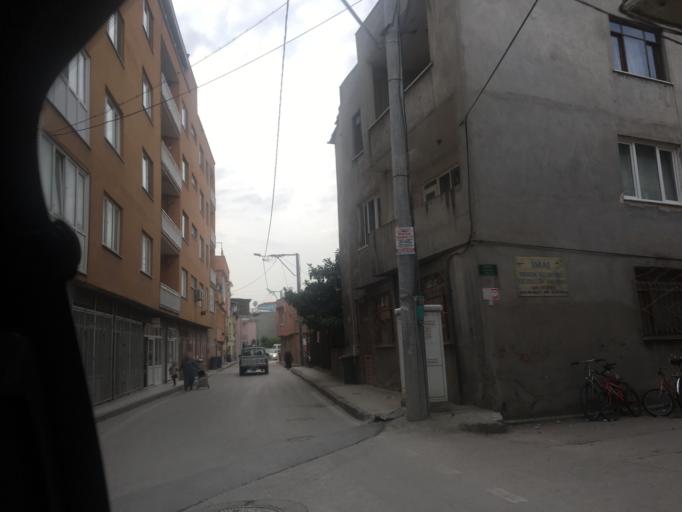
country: TR
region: Bursa
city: Yildirim
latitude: 40.2092
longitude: 29.0313
